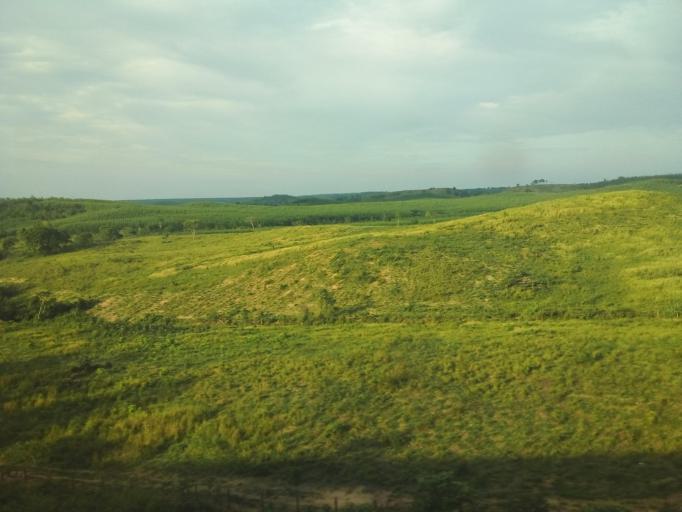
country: BR
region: Maranhao
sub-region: Imperatriz
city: Imperatriz
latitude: -4.8080
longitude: -47.3218
